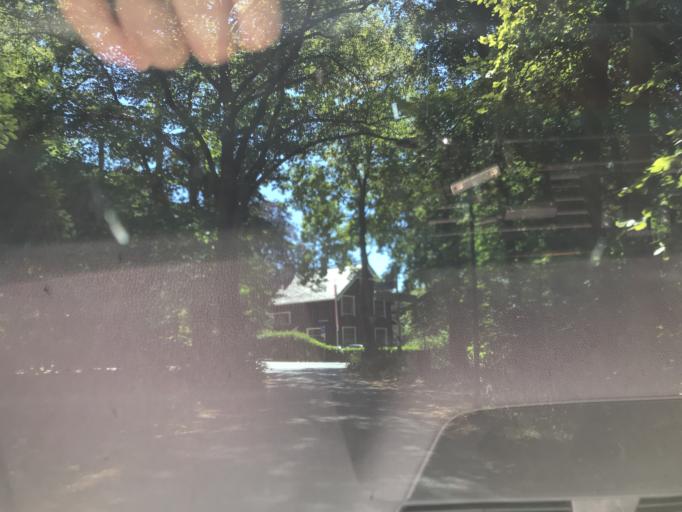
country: NL
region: North Holland
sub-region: Gemeente Naarden
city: Naarden
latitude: 52.2933
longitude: 5.1904
